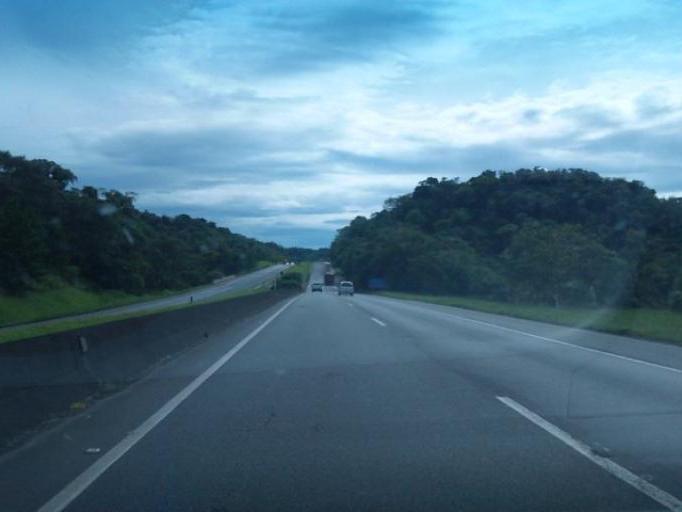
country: BR
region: Sao Paulo
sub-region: Cajati
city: Cajati
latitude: -24.9605
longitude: -48.3382
